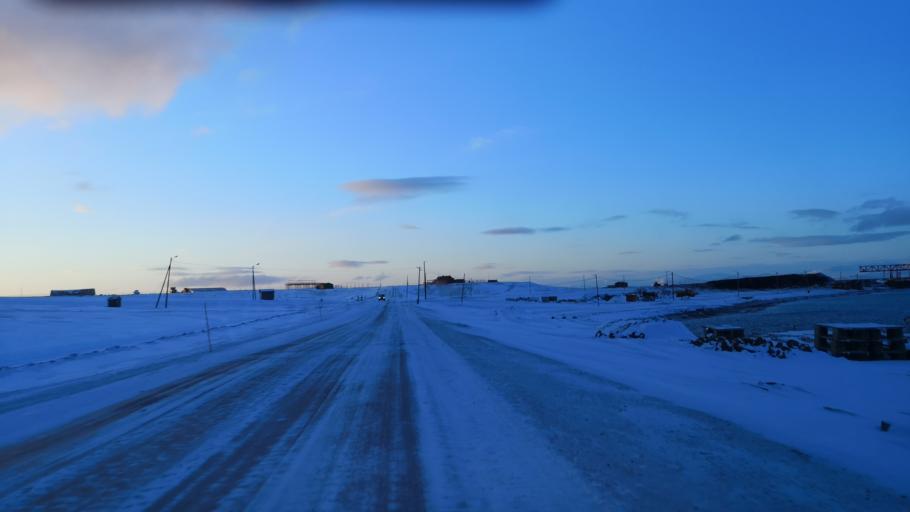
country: SJ
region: Svalbard
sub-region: Spitsbergen
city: Longyearbyen
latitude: 78.2387
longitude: 15.5379
